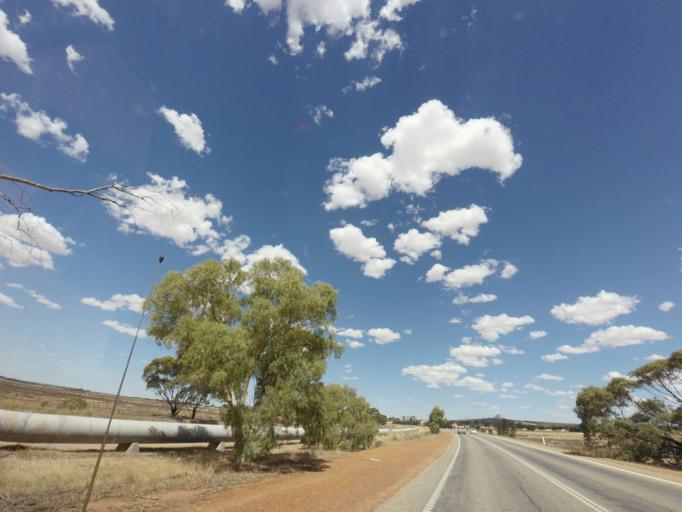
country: AU
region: Western Australia
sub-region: Cunderdin
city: Cunderdin
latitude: -31.6502
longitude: 117.2018
